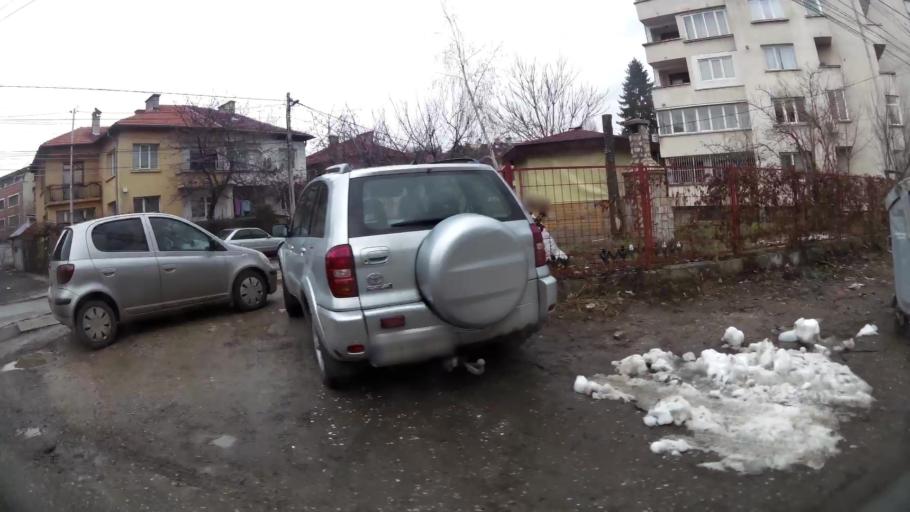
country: BG
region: Sofia-Capital
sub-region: Stolichna Obshtina
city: Sofia
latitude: 42.6689
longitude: 23.2518
